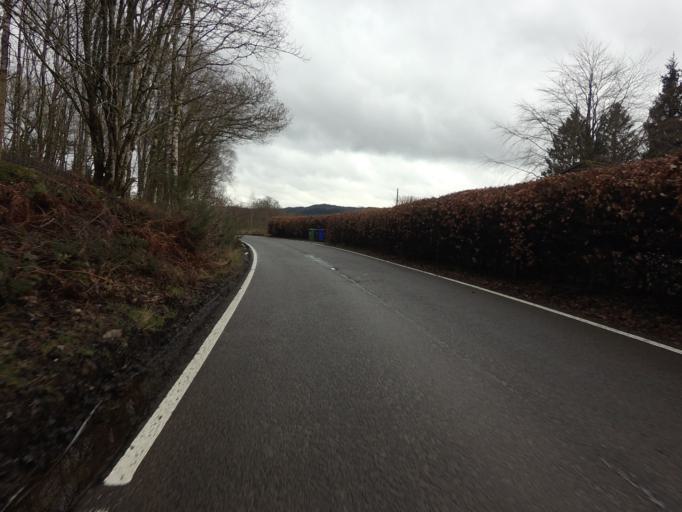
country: GB
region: Scotland
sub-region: Stirling
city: Killearn
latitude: 56.1894
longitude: -4.4968
